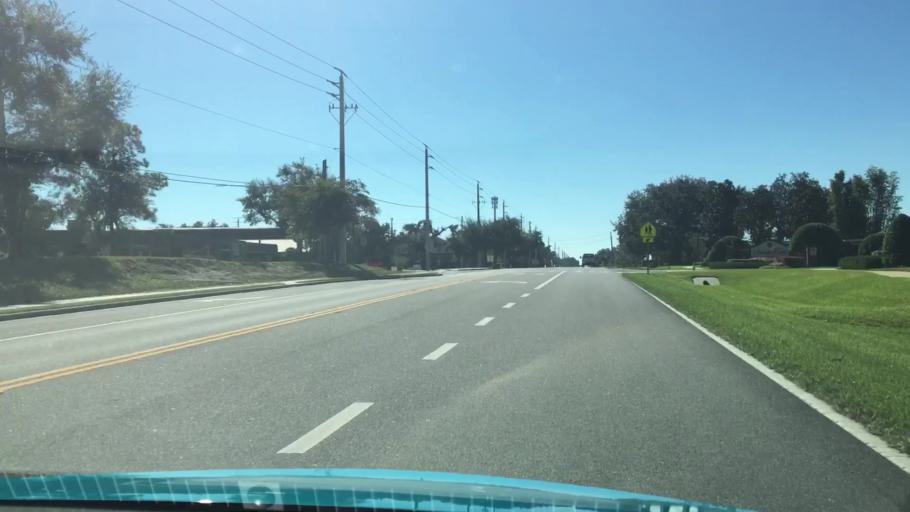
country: US
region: Florida
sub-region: Seminole County
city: Heathrow
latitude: 28.8027
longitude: -81.3630
